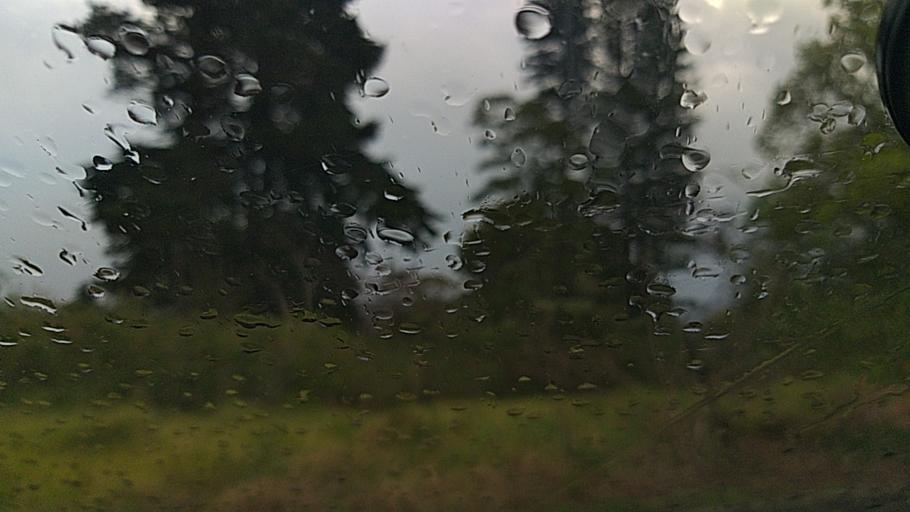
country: AU
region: New South Wales
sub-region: Wollongong
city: Dapto
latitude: -34.4959
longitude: 150.7888
